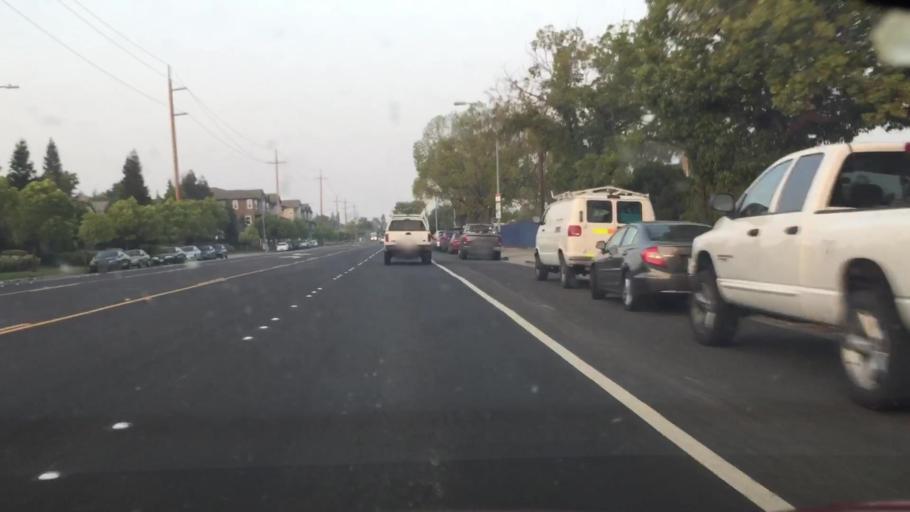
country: US
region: California
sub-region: Alameda County
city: Livermore
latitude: 37.6887
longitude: -121.7567
